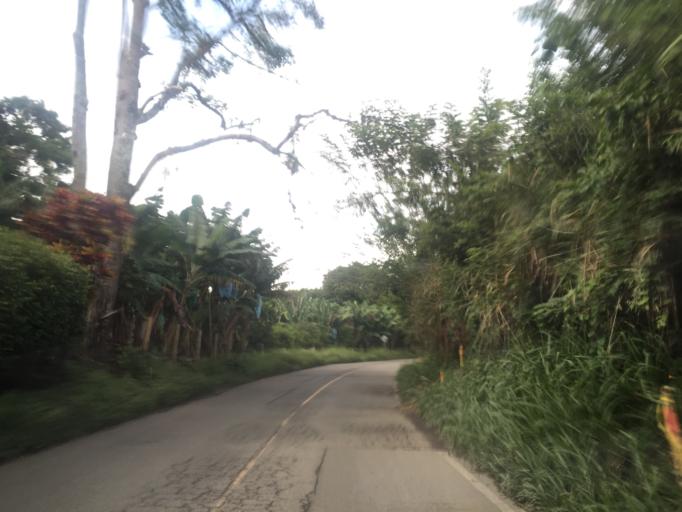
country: CO
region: Quindio
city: La Tebaida
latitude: 4.4703
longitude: -75.8137
